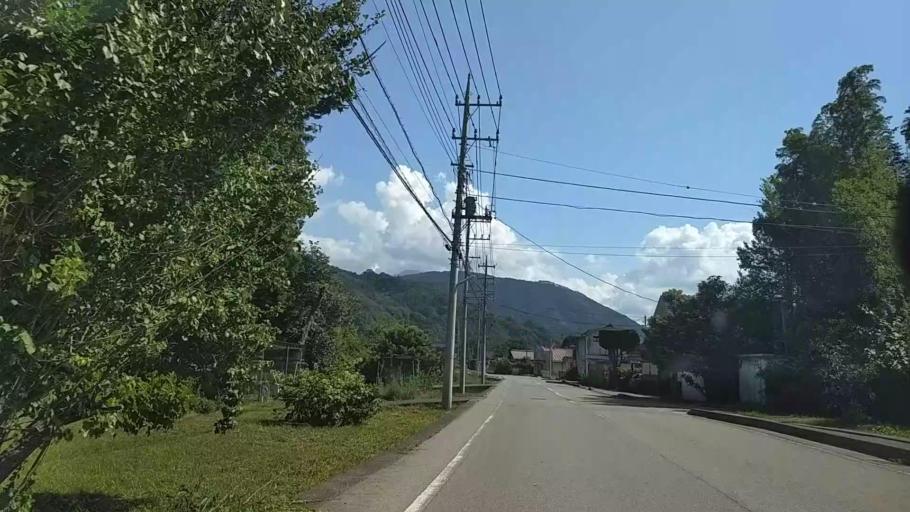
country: JP
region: Yamanashi
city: Ryuo
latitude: 35.4628
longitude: 138.4442
